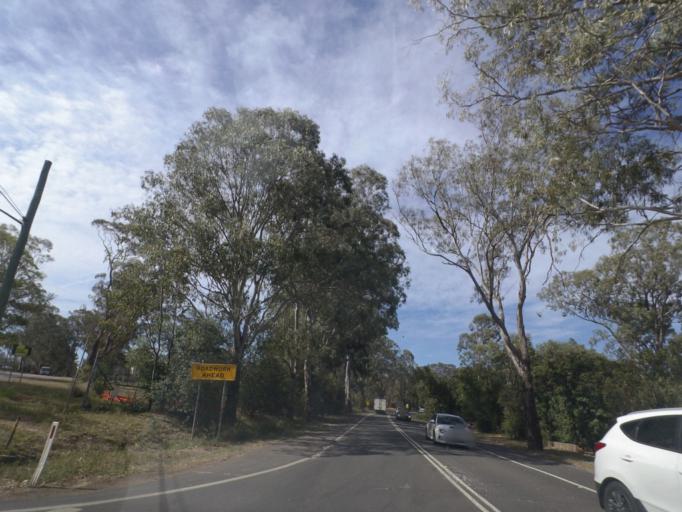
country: AU
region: New South Wales
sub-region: Campbelltown Municipality
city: Denham Court
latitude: -33.9780
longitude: 150.8502
